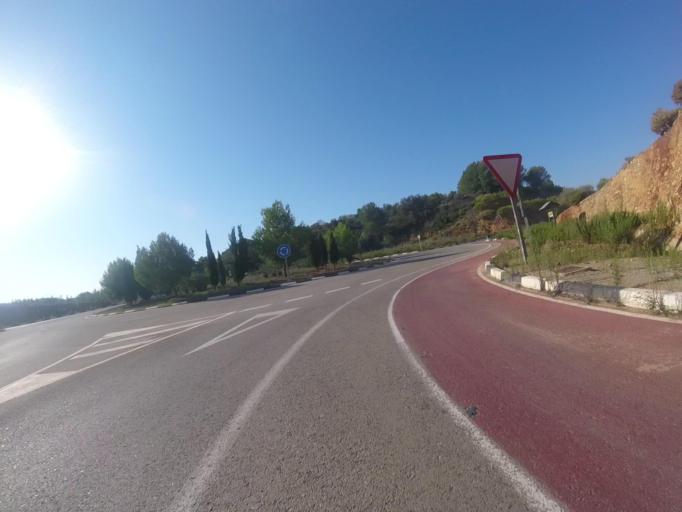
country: ES
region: Valencia
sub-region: Provincia de Castello
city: Benlloch
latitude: 40.1957
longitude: 0.0532
